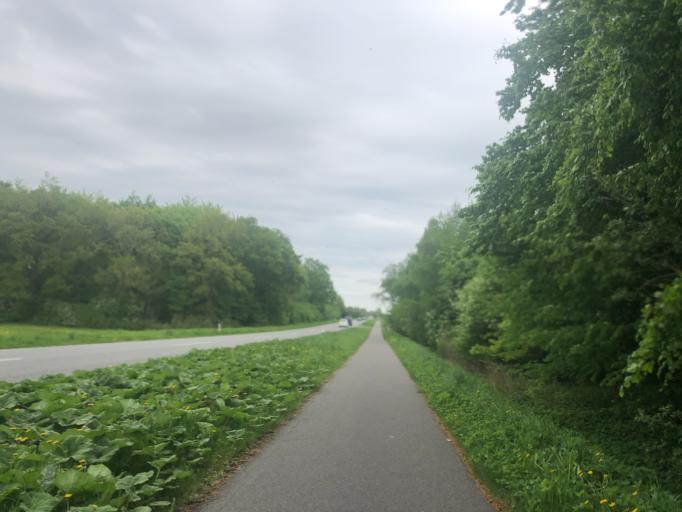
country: DK
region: Zealand
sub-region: Koge Kommune
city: Borup
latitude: 55.4471
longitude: 11.9258
